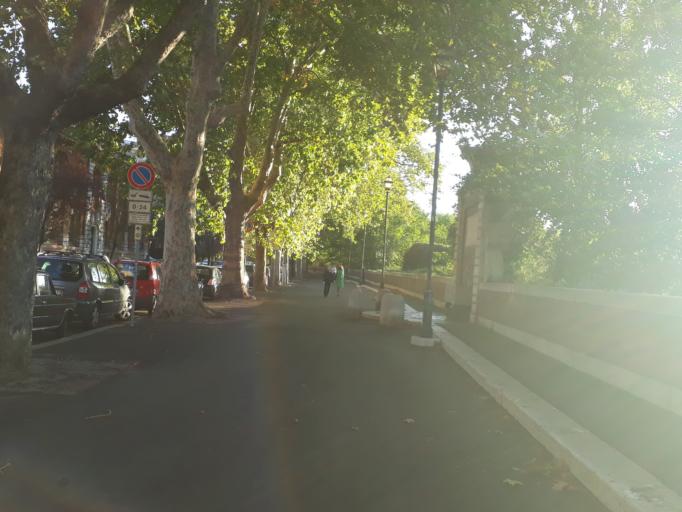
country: VA
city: Vatican City
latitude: 41.8804
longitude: 12.4722
